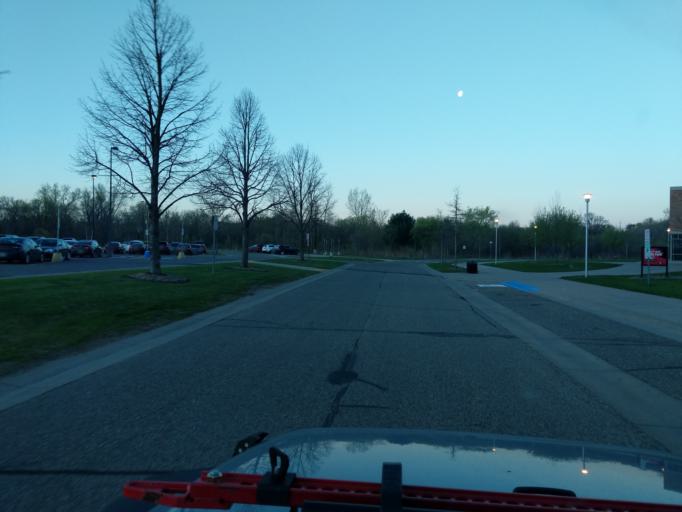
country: US
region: Wisconsin
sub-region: Pierce County
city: River Falls
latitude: 44.8509
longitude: -92.6143
